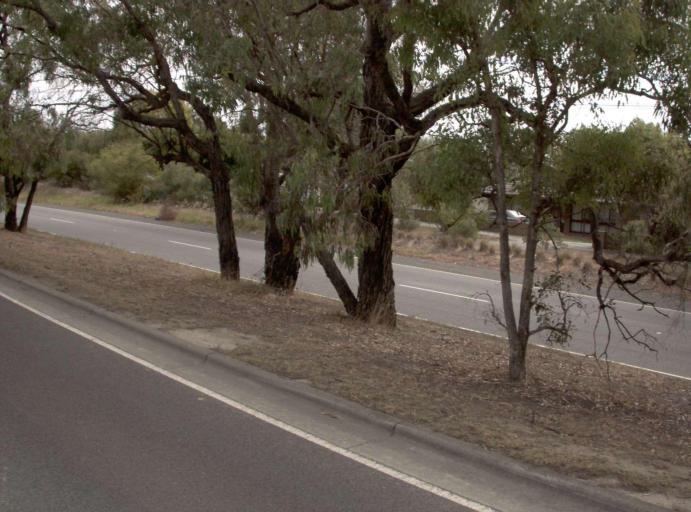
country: AU
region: Victoria
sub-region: Knox
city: Rowville
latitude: -37.9207
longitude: 145.2346
